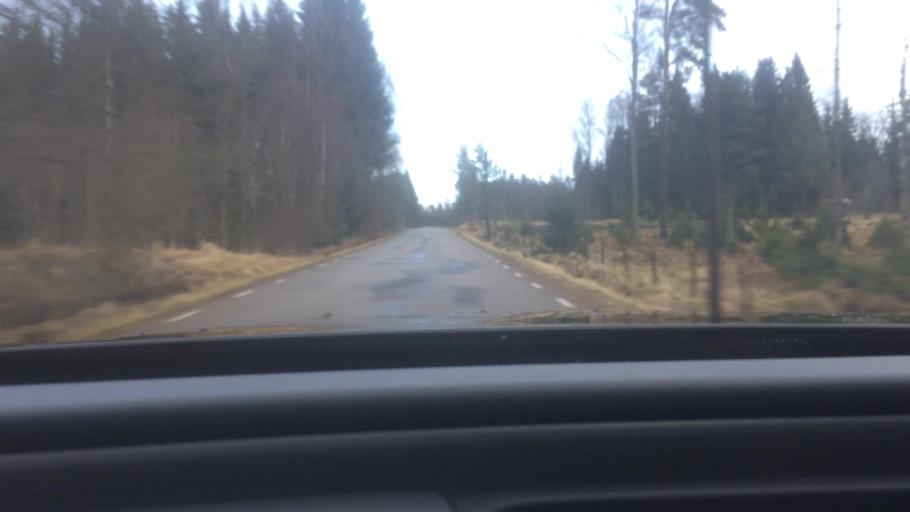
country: SE
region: Vaestra Goetaland
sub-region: Falkopings Kommun
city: Falkoeping
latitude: 57.9956
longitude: 13.4757
